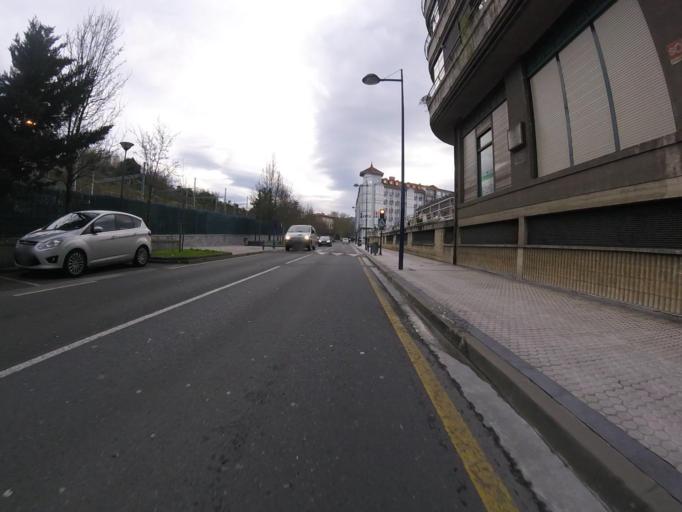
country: ES
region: Basque Country
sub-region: Provincia de Guipuzcoa
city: Errenteria
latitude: 43.3111
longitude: -1.8926
